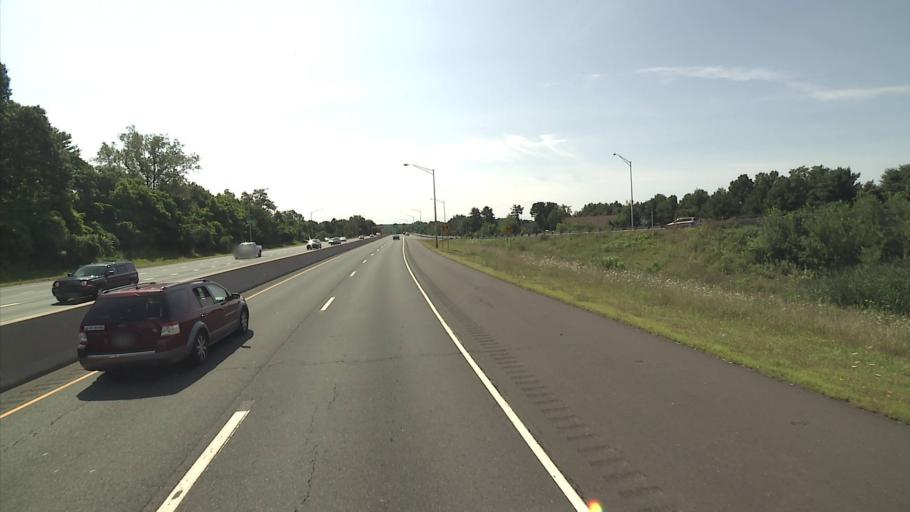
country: US
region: Connecticut
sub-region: Hartford County
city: Glastonbury
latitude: 41.7257
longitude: -72.6101
